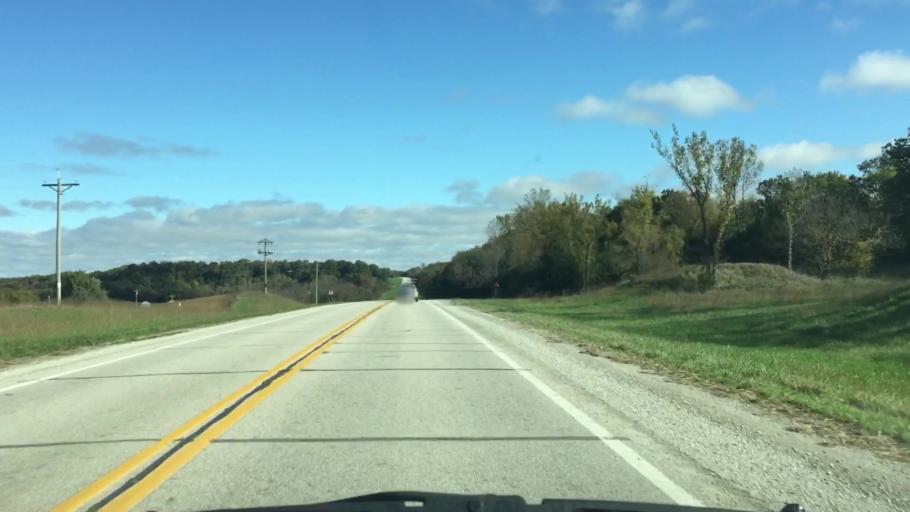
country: US
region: Iowa
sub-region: Decatur County
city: Leon
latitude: 40.6498
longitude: -93.8020
